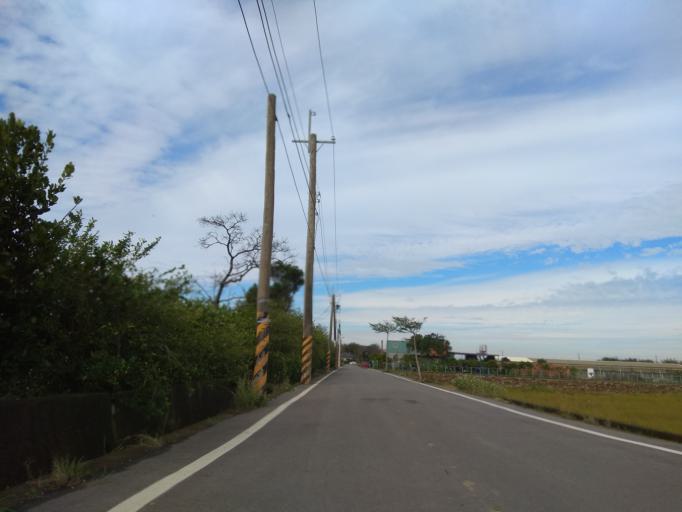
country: TW
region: Taiwan
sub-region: Hsinchu
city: Zhubei
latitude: 24.9526
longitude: 121.1088
